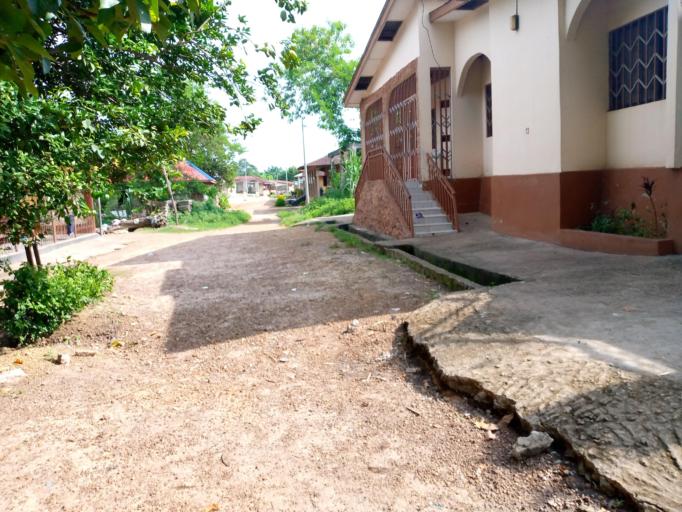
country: SL
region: Northern Province
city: Magburaka
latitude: 8.7257
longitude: -11.9472
